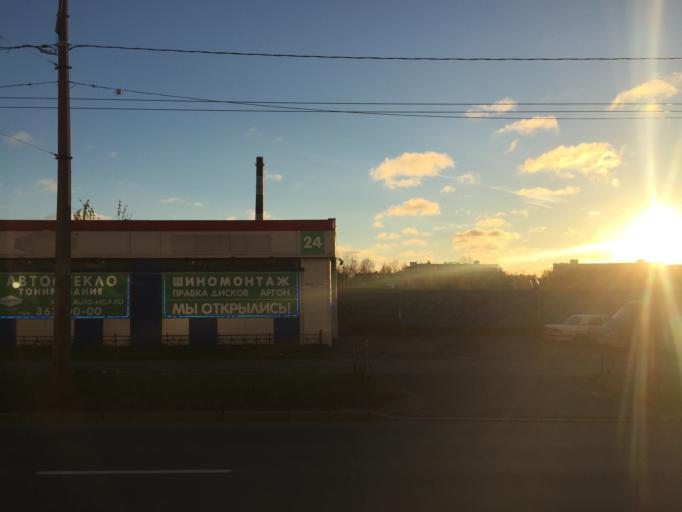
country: RU
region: St.-Petersburg
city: Centralniy
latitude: 59.9166
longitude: 30.4291
